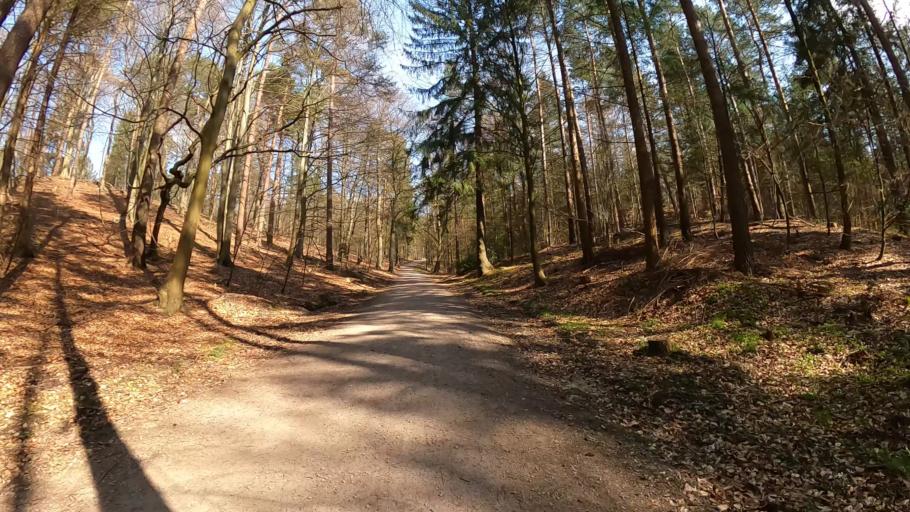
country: DE
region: Hamburg
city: Harburg
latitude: 53.4643
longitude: 9.9034
